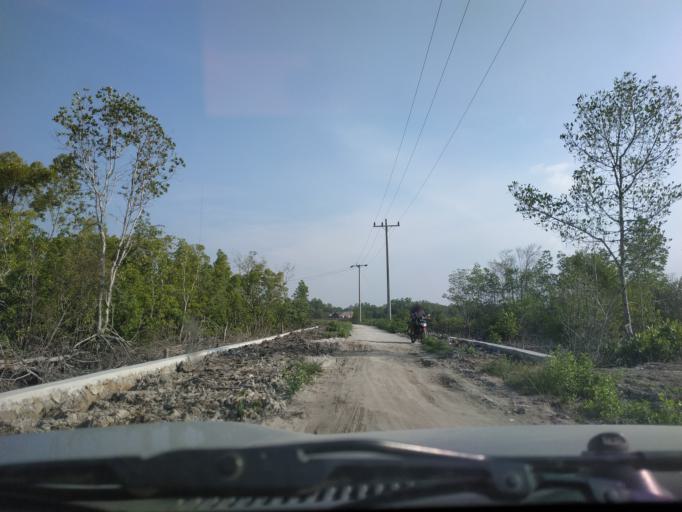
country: ID
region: North Sumatra
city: Teluk Nibung
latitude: 3.1081
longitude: 99.7786
